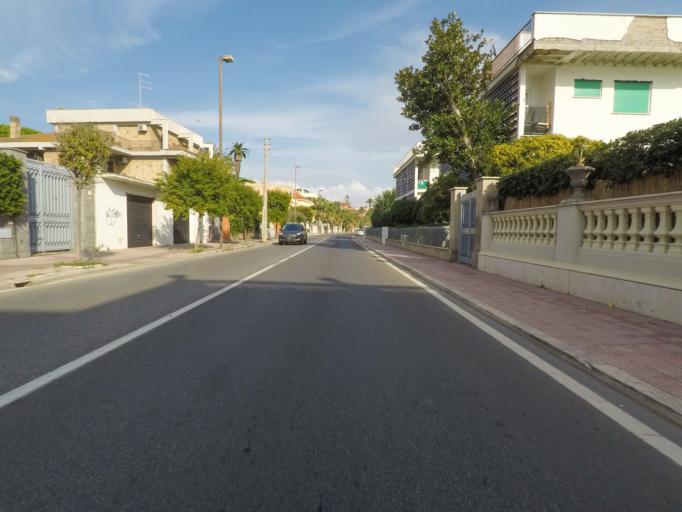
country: IT
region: Latium
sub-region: Citta metropolitana di Roma Capitale
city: Santa Marinella
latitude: 42.0342
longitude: 11.8579
